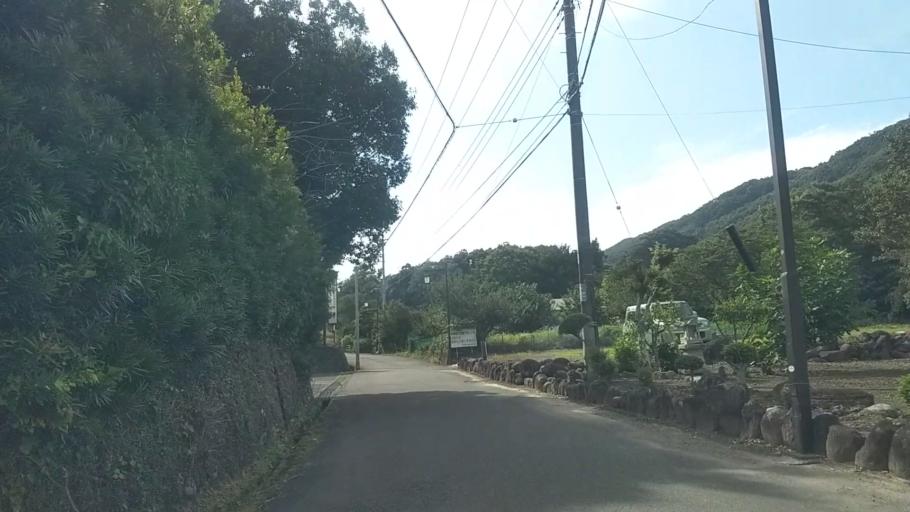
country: JP
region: Shizuoka
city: Heda
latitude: 34.9692
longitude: 138.9217
